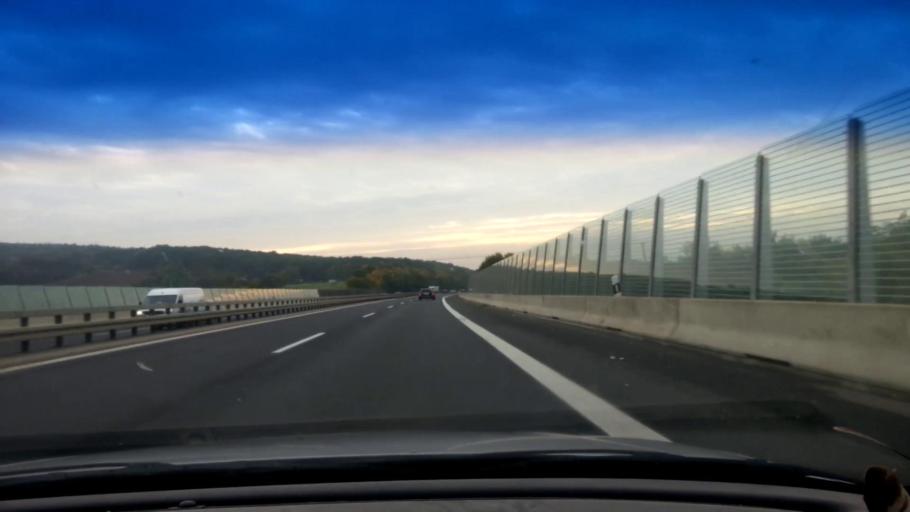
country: DE
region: Bavaria
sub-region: Upper Franconia
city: Zapfendorf
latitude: 50.0101
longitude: 10.9322
